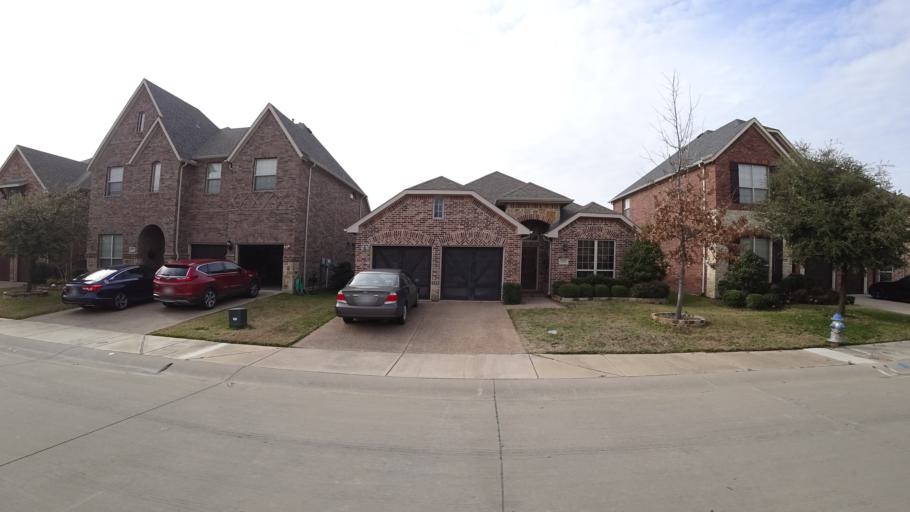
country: US
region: Texas
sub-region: Denton County
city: The Colony
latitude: 33.0520
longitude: -96.9084
